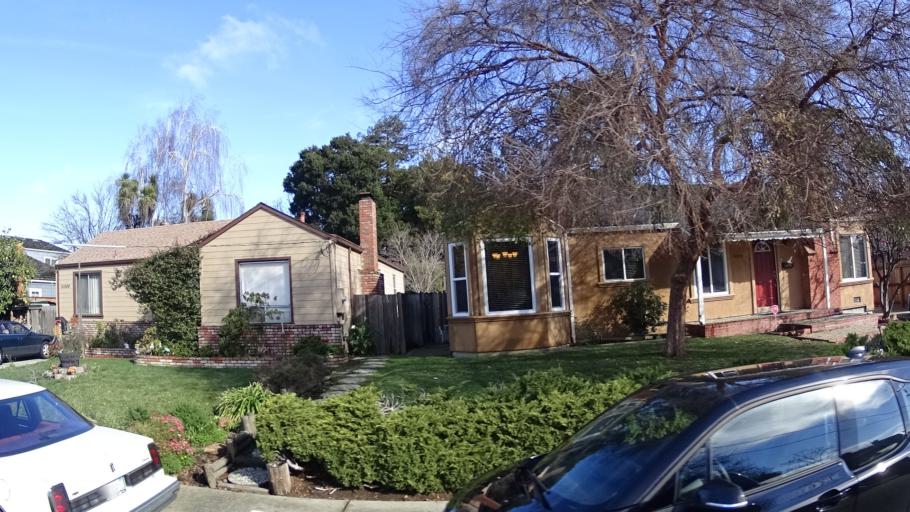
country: US
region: California
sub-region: Alameda County
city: Castro Valley
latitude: 37.6871
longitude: -122.0807
